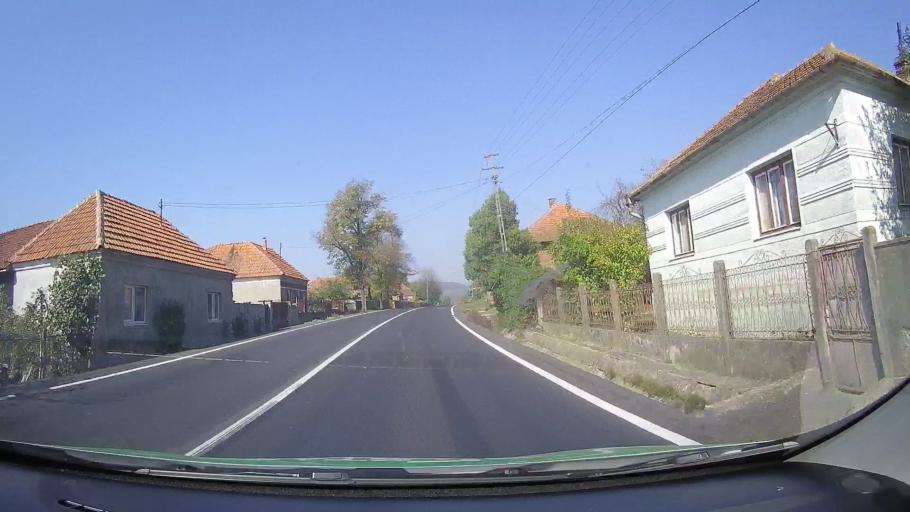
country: RO
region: Hunedoara
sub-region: Comuna Burjuc
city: Burjuc
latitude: 45.9476
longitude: 22.4925
